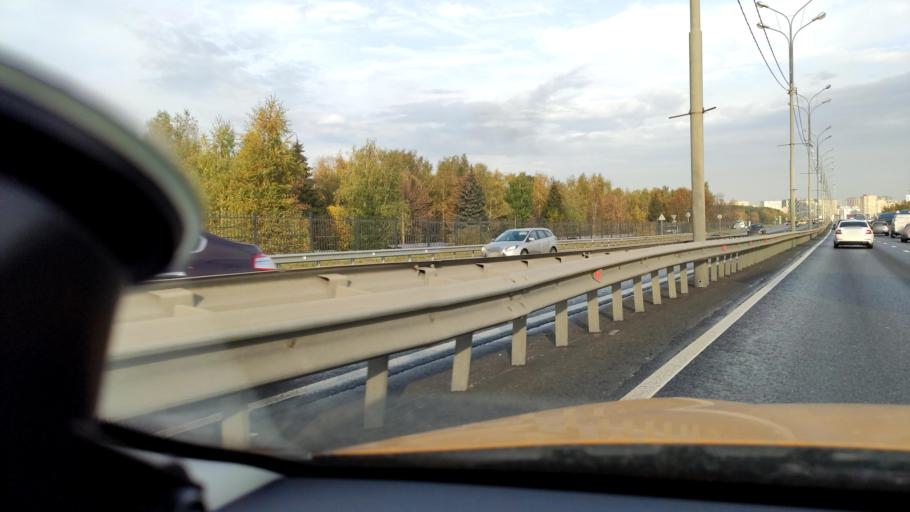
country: RU
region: Moscow
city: Vatutino
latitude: 55.9203
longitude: 37.6922
